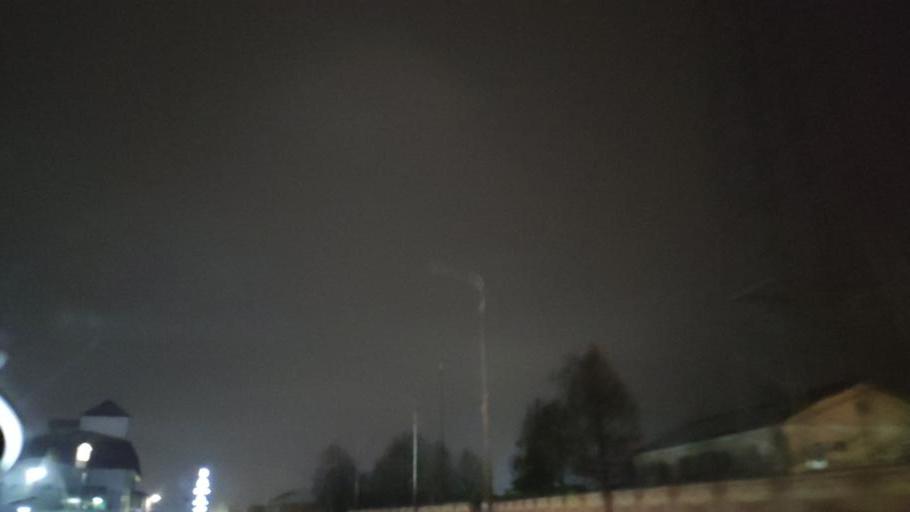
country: RU
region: Moskovskaya
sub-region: Podol'skiy Rayon
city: Podol'sk
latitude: 55.4361
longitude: 37.6020
